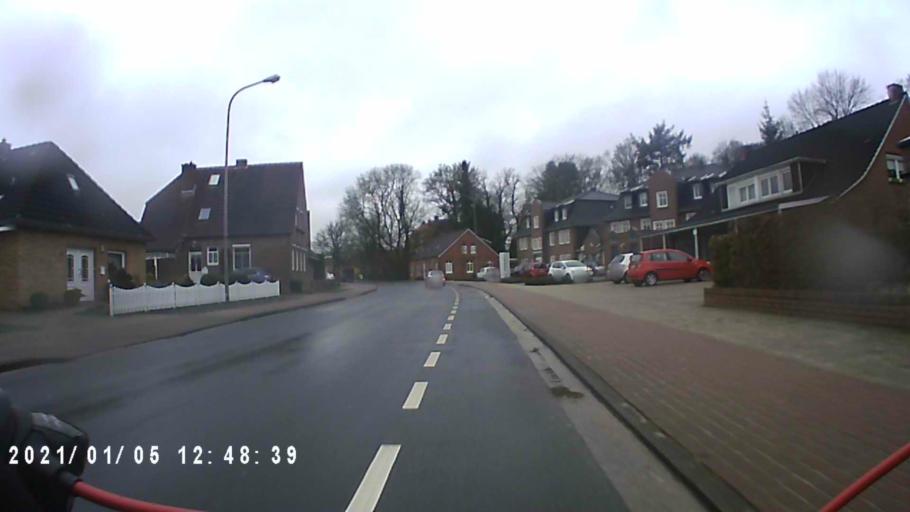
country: DE
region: Lower Saxony
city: Leer
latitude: 53.2391
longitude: 7.4983
